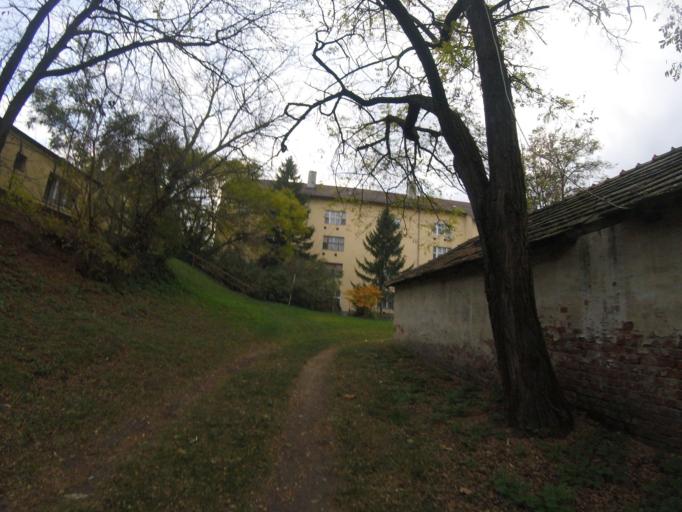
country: HU
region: Fejer
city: Szekesfehervar
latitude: 47.1595
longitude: 18.4102
